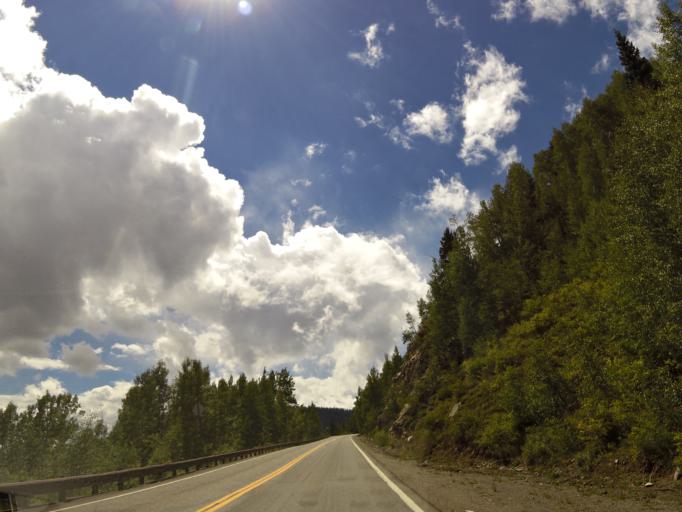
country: US
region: Colorado
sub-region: San Juan County
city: Silverton
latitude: 37.7146
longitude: -107.7550
